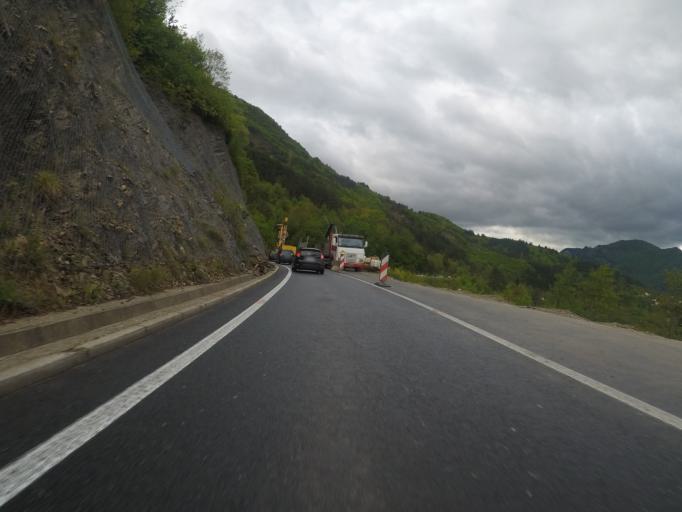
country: BA
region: Federation of Bosnia and Herzegovina
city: Jablanica
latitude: 43.6457
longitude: 17.7578
